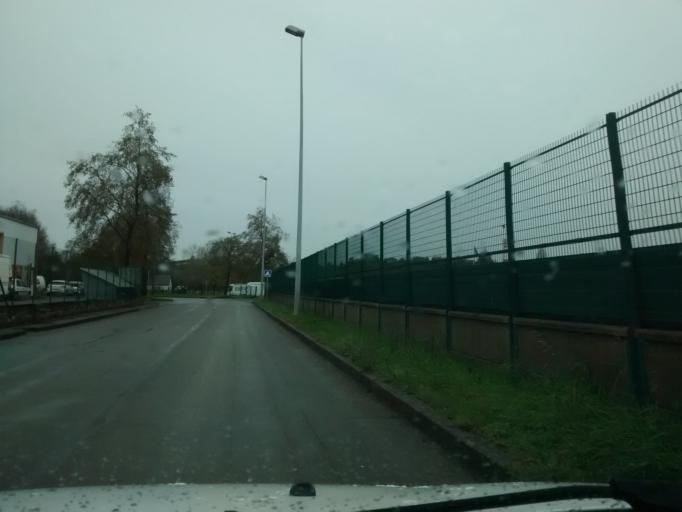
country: FR
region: Brittany
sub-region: Departement d'Ille-et-Vilaine
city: Chantepie
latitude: 48.1102
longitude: -1.6369
